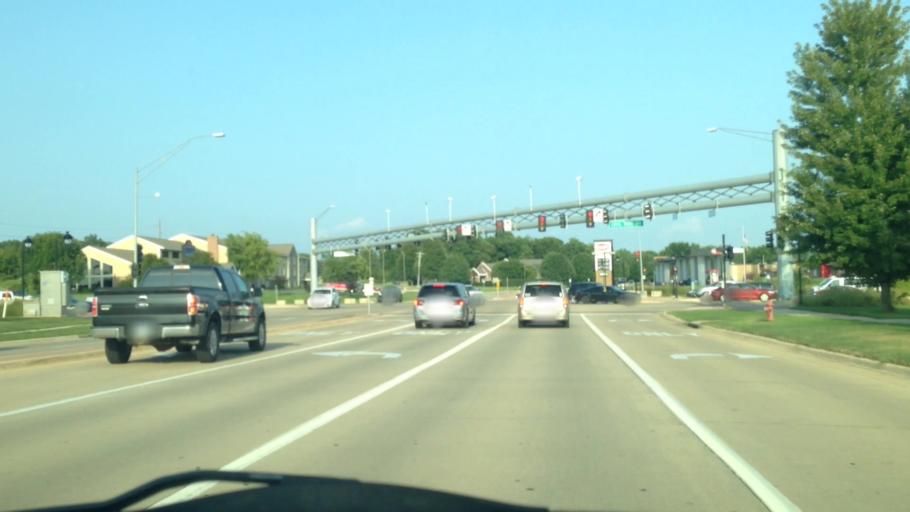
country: US
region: Iowa
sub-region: Johnson County
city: Coralville
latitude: 41.7004
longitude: -91.6094
